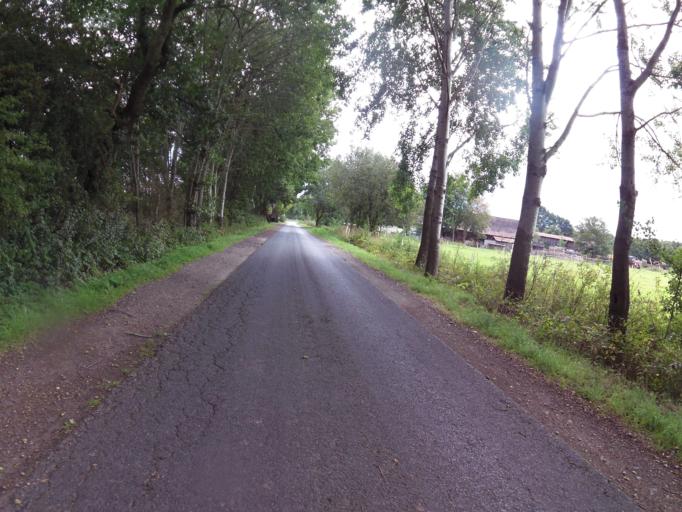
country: DE
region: Lower Saxony
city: Schiffdorf
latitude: 53.5008
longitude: 8.7020
